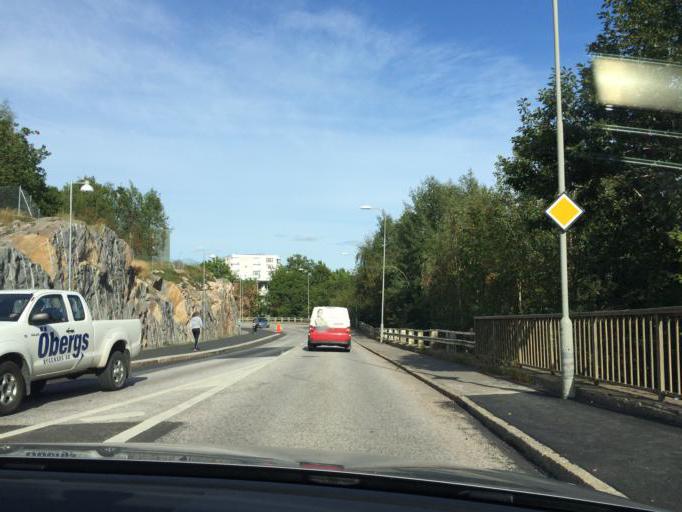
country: SE
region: Vaestra Goetaland
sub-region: Goteborg
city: Goeteborg
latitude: 57.6788
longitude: 11.9835
